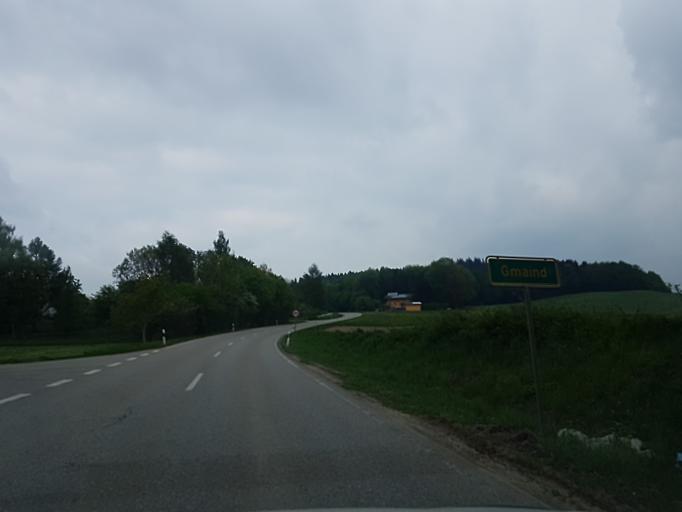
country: DE
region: Bavaria
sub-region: Upper Bavaria
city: Ebersberg
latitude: 48.0939
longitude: 11.9752
